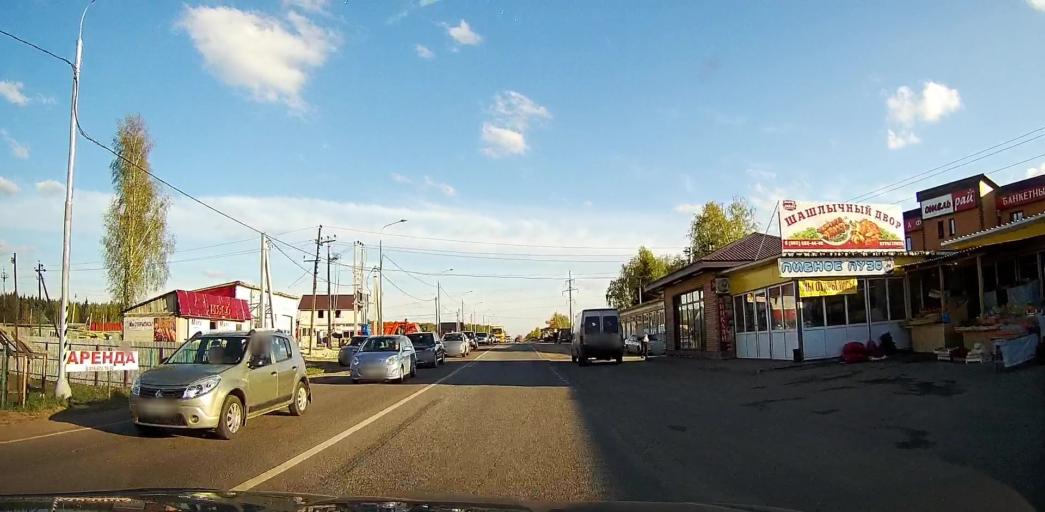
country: RU
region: Moskovskaya
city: Bronnitsy
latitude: 55.3878
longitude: 38.2058
